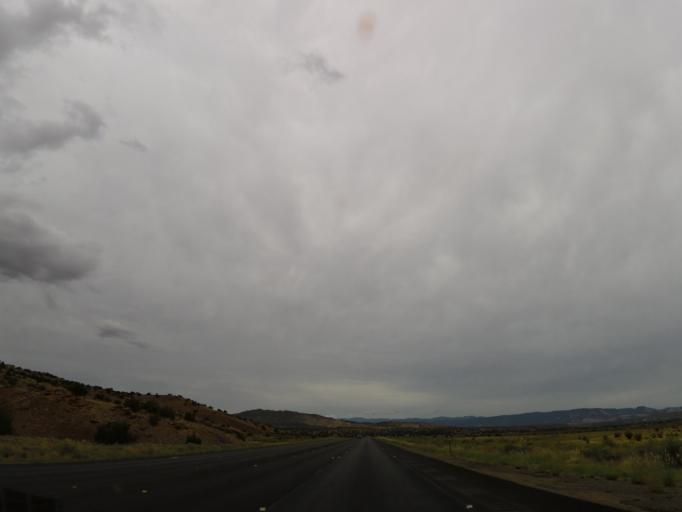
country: US
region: New Mexico
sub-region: Sandoval County
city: Jemez Pueblo
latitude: 35.5443
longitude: -106.8294
